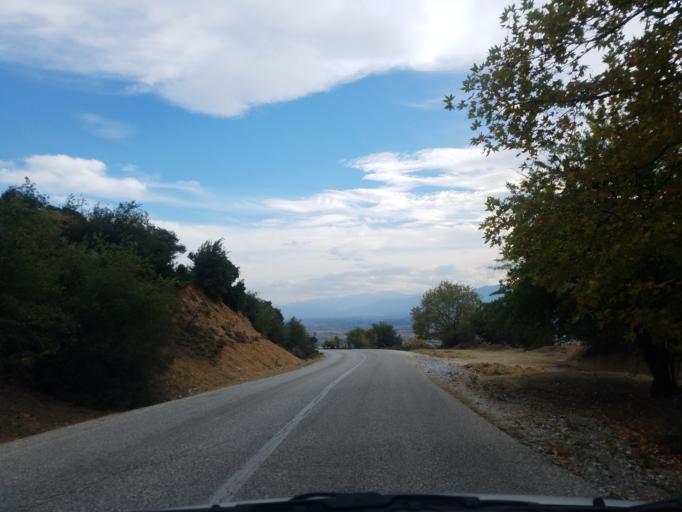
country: GR
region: Thessaly
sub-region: Trikala
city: Kalampaka
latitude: 39.7153
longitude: 21.6492
